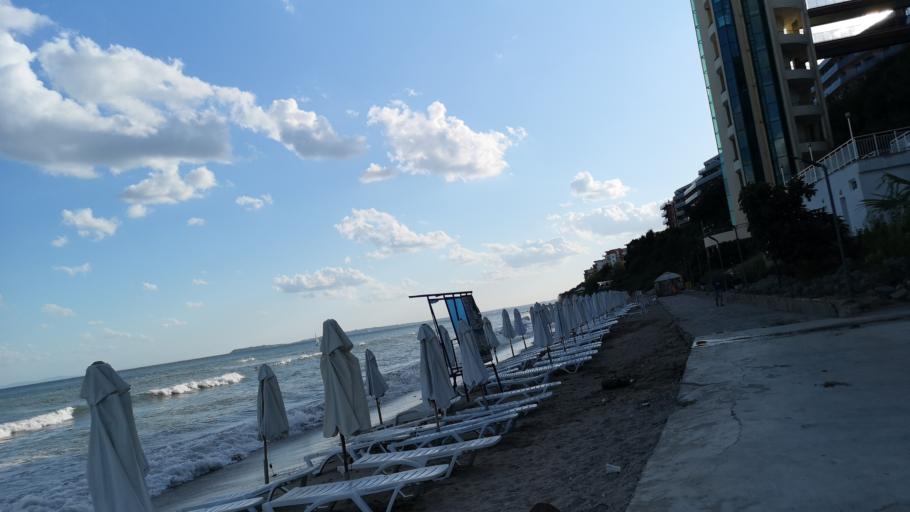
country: BG
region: Burgas
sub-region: Obshtina Nesebur
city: Sveti Vlas
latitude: 42.7041
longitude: 27.8007
